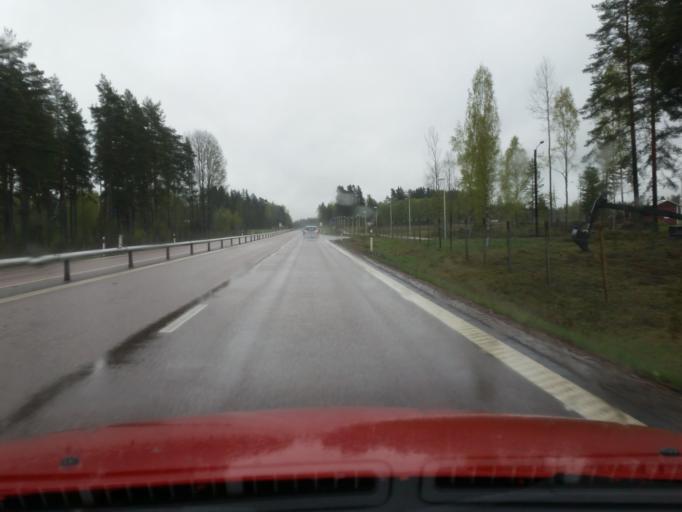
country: SE
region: Dalarna
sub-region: Saters Kommun
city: Saeter
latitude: 60.3368
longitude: 15.7850
